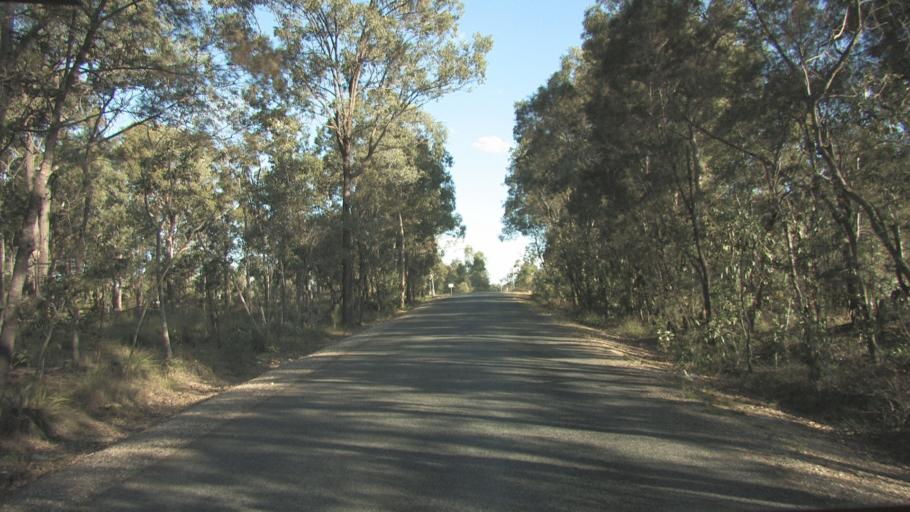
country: AU
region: Queensland
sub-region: Ipswich
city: Springfield Lakes
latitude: -27.6935
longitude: 152.9377
